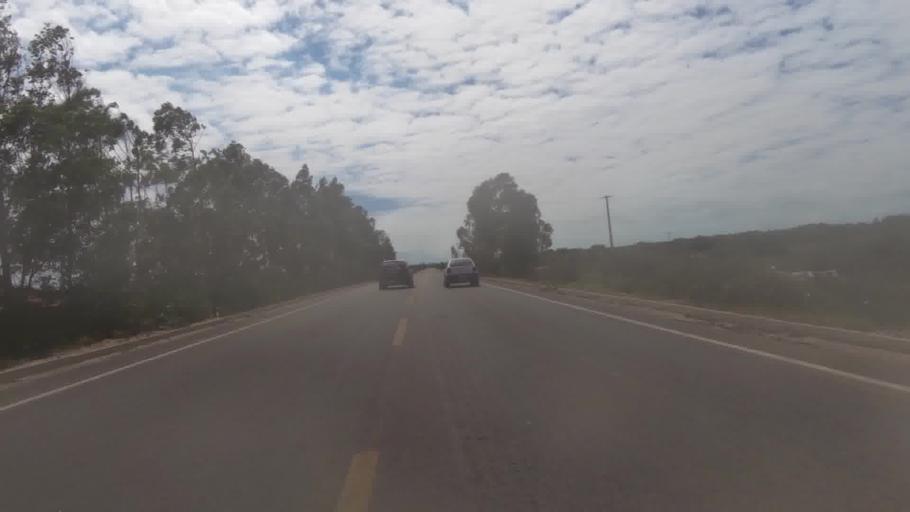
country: BR
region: Espirito Santo
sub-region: Marataizes
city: Marataizes
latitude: -21.2247
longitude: -40.9718
